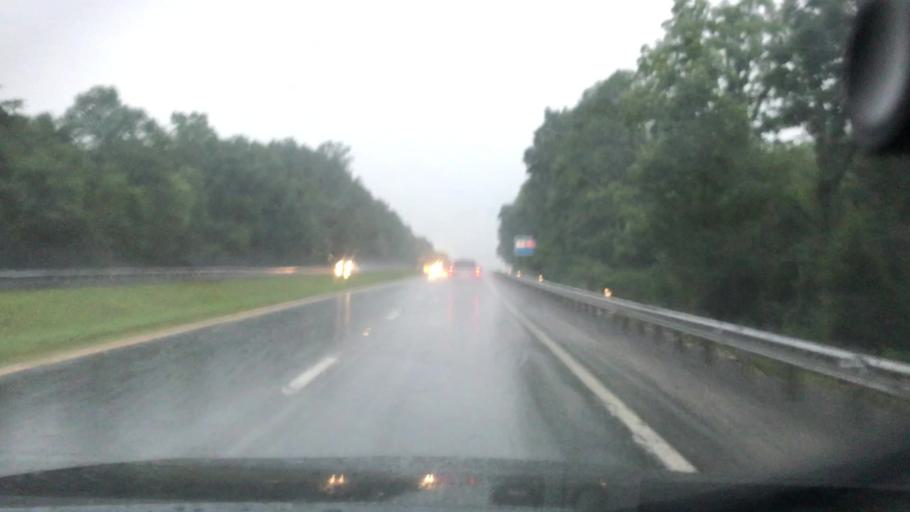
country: US
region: Virginia
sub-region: Giles County
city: Pearisburg
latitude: 37.3377
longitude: -80.7108
